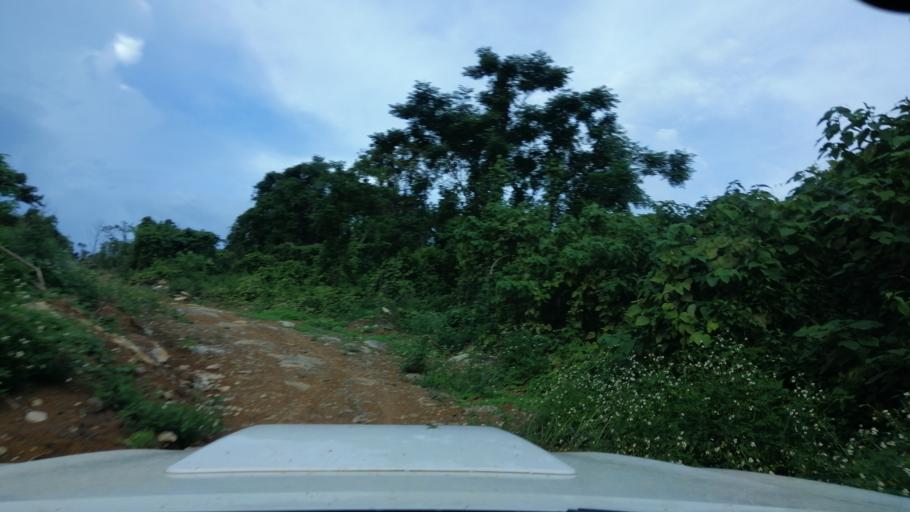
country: TH
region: Nan
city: Chaloem Phra Kiat
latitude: 19.7590
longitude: 101.1162
